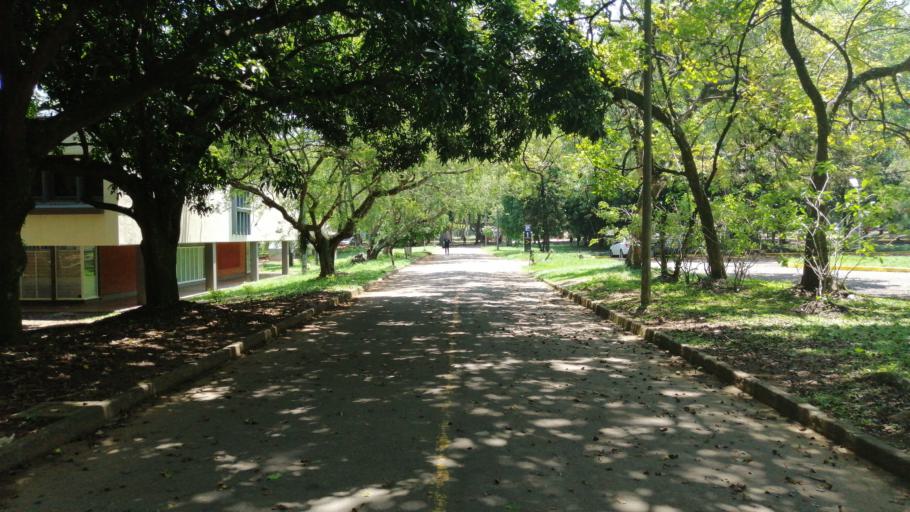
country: CO
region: Valle del Cauca
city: Cali
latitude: 3.3749
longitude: -76.5333
